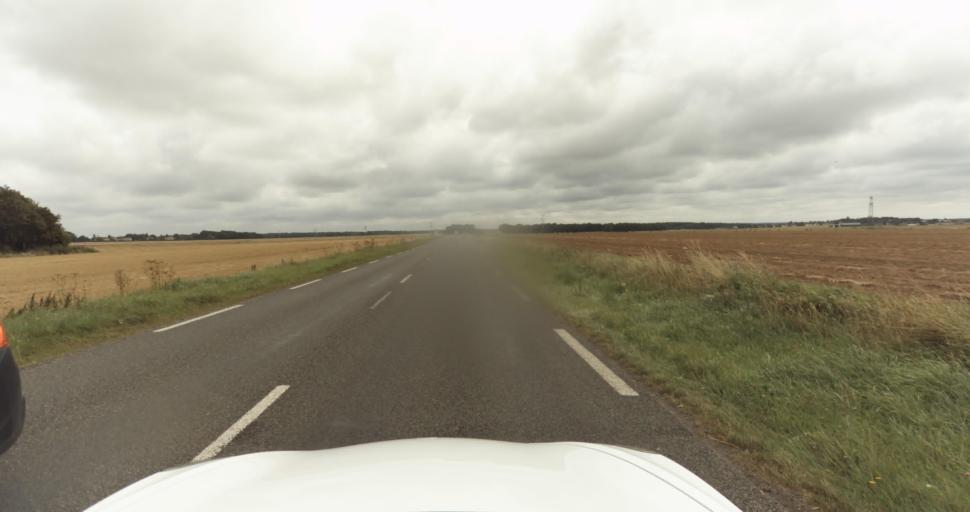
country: FR
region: Haute-Normandie
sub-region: Departement de l'Eure
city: Claville
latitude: 49.0400
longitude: 1.0255
